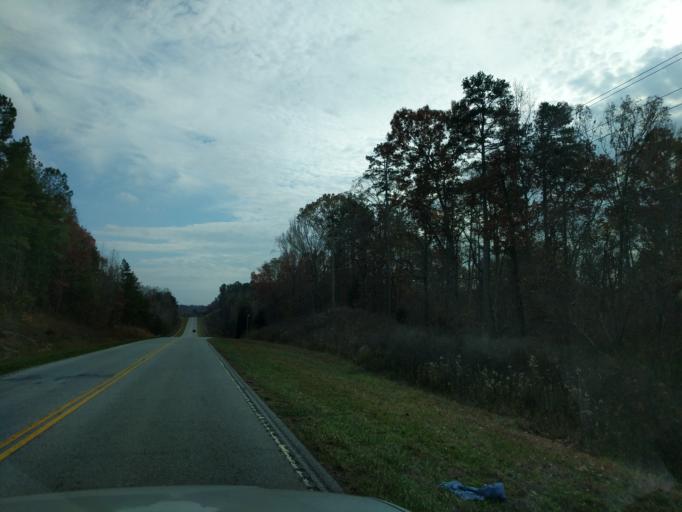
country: US
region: Georgia
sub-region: Franklin County
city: Gumlog
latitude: 34.5100
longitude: -83.0434
